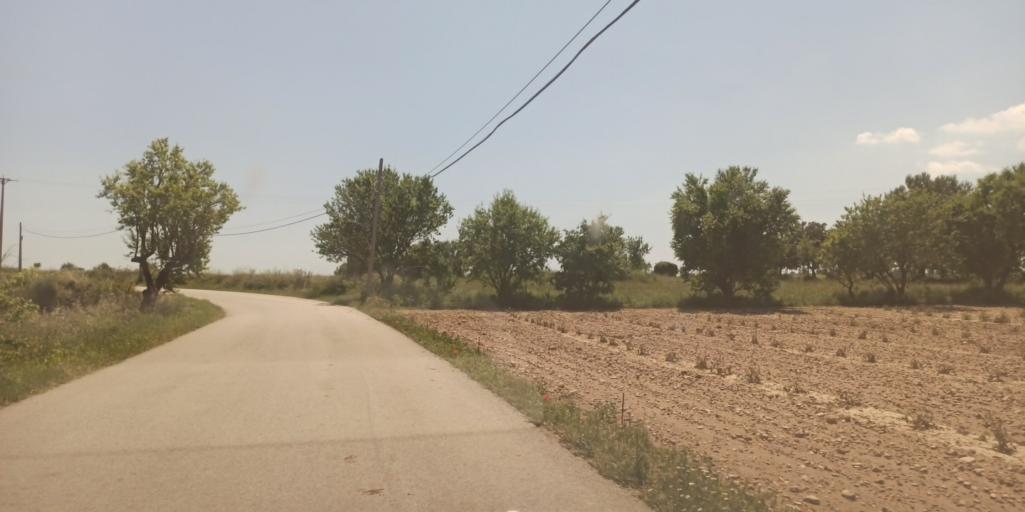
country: ES
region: Catalonia
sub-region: Provincia de Barcelona
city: Vilobi del Penedes
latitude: 41.3528
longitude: 1.6481
